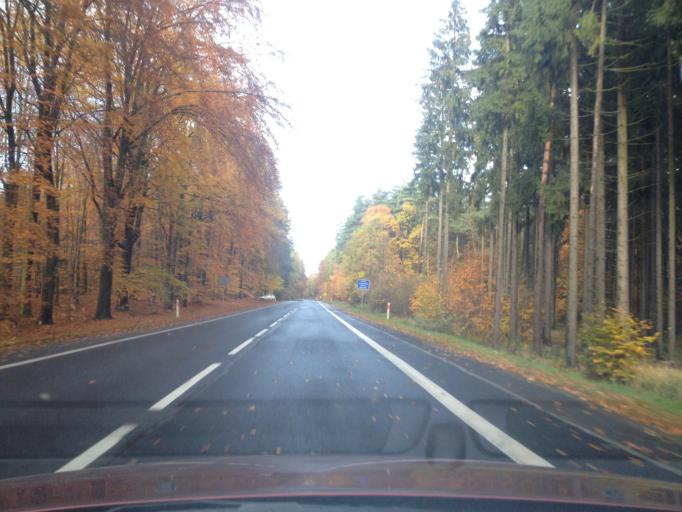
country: PL
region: Lower Silesian Voivodeship
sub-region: Powiat lubanski
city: Siekierczyn
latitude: 51.1575
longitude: 15.1521
